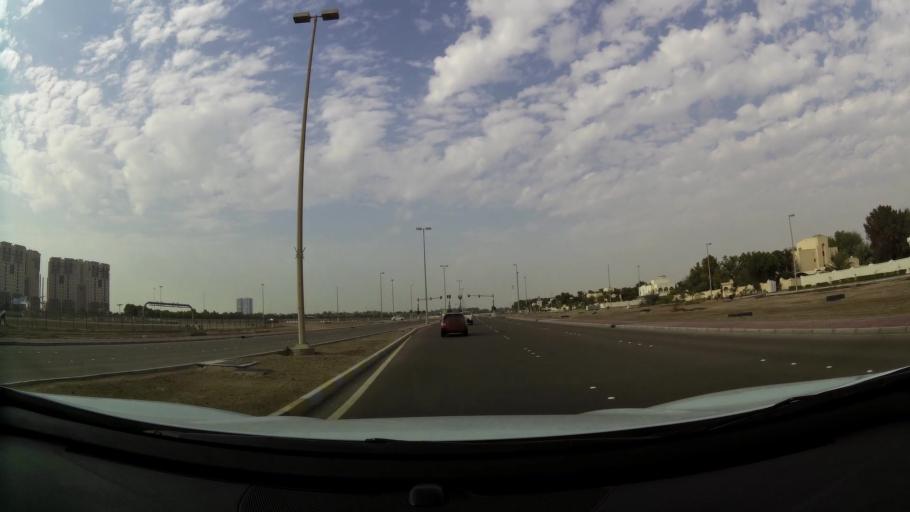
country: AE
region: Abu Dhabi
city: Abu Dhabi
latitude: 24.3817
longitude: 54.5273
